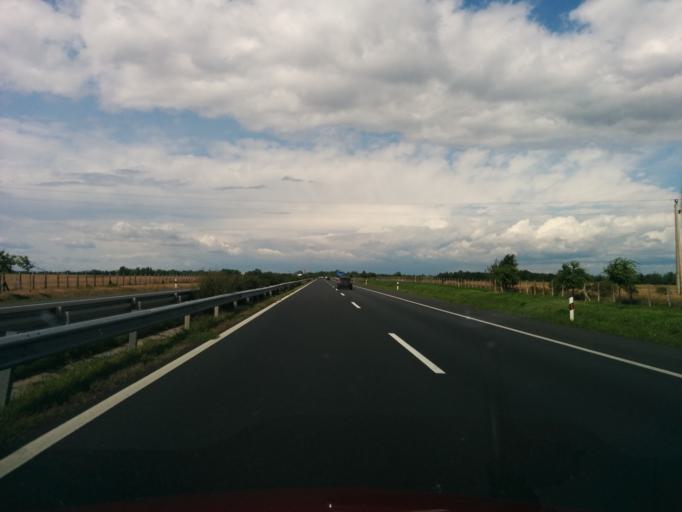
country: HU
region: Gyor-Moson-Sopron
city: Mosonmagyarovar
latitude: 47.8927
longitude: 17.1797
